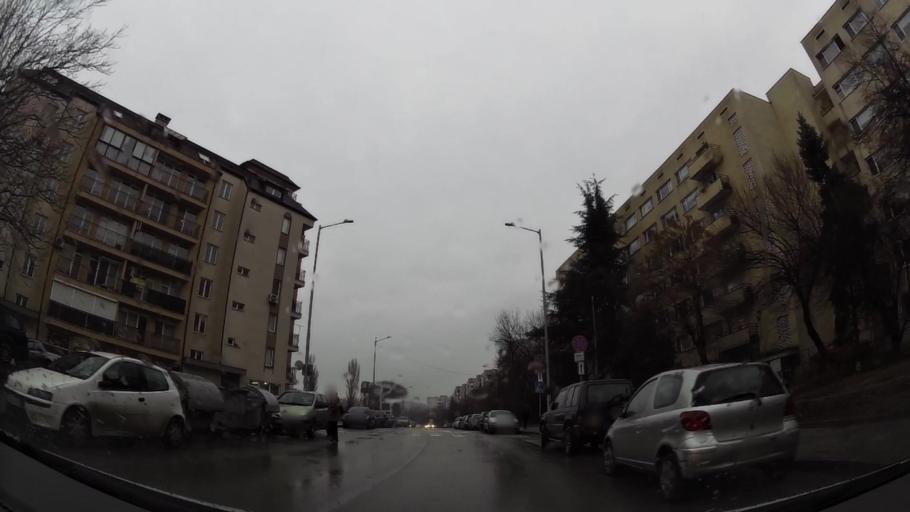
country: BG
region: Sofia-Capital
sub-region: Stolichna Obshtina
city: Sofia
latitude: 42.6579
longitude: 23.3635
